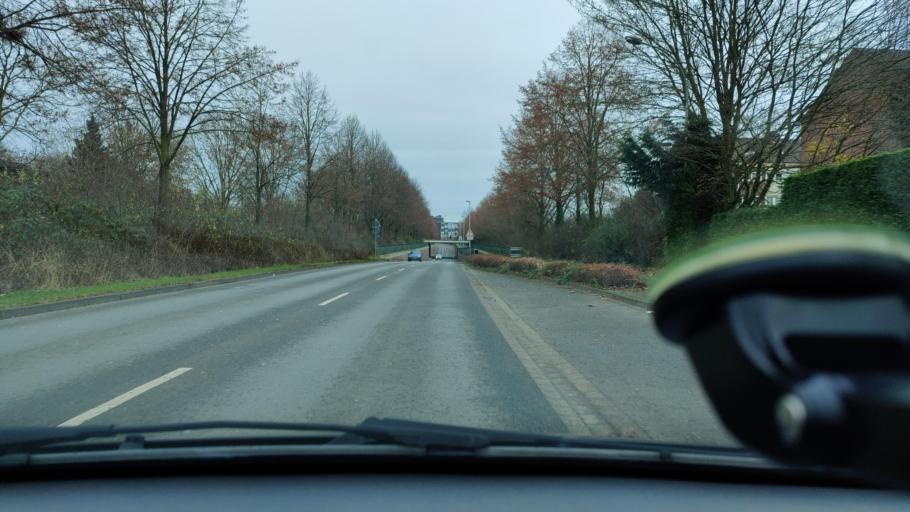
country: DE
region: North Rhine-Westphalia
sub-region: Regierungsbezirk Dusseldorf
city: Weeze
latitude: 51.6253
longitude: 6.1933
